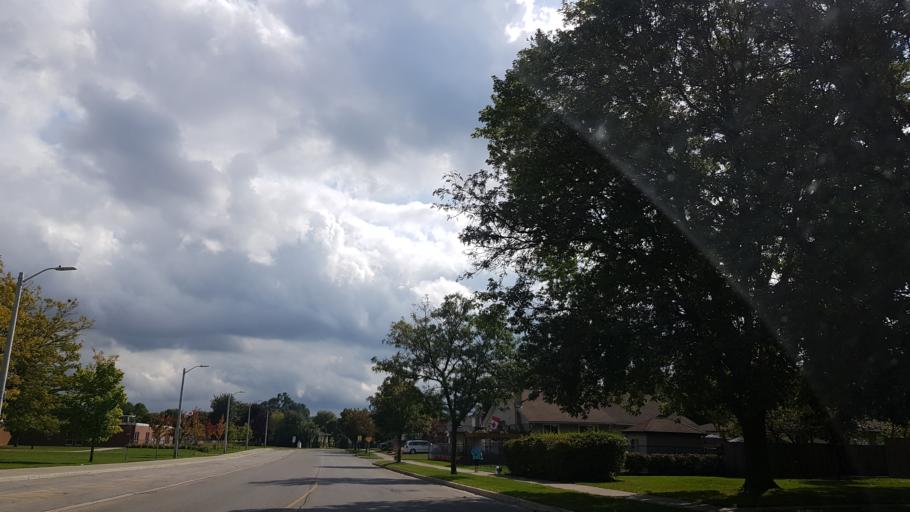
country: CA
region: Ontario
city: London
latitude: 42.9322
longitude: -81.2366
